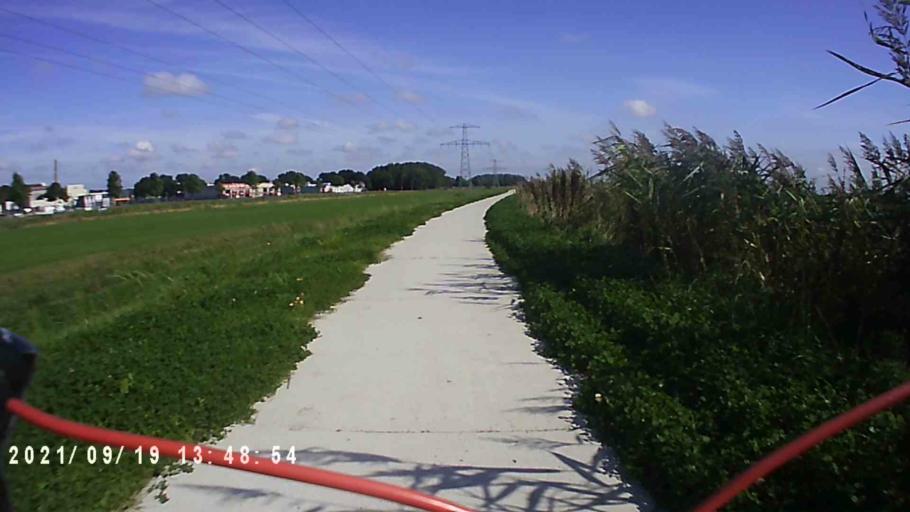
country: NL
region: Groningen
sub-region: Gemeente  Oldambt
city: Winschoten
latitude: 53.1317
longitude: 7.0544
